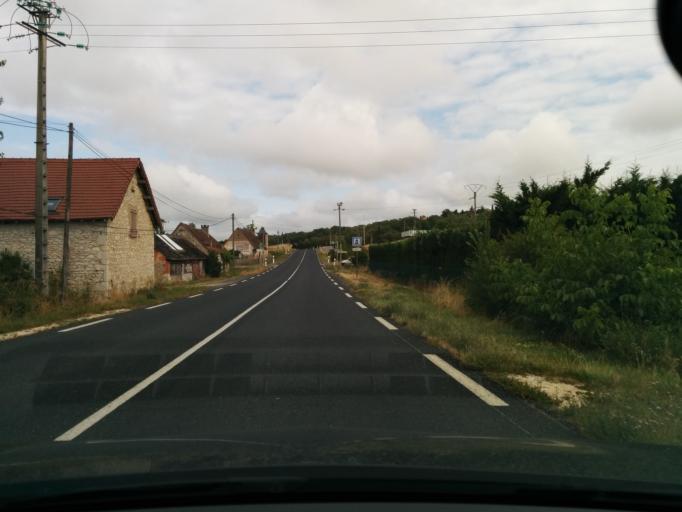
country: FR
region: Midi-Pyrenees
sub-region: Departement du Lot
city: Le Vigan
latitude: 44.7470
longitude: 1.4999
